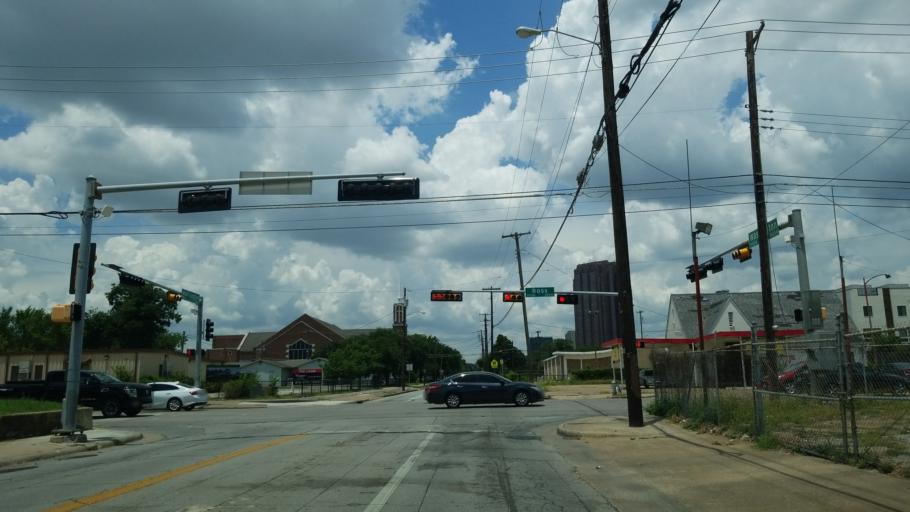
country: US
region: Texas
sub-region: Dallas County
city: Dallas
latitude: 32.7977
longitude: -96.7859
